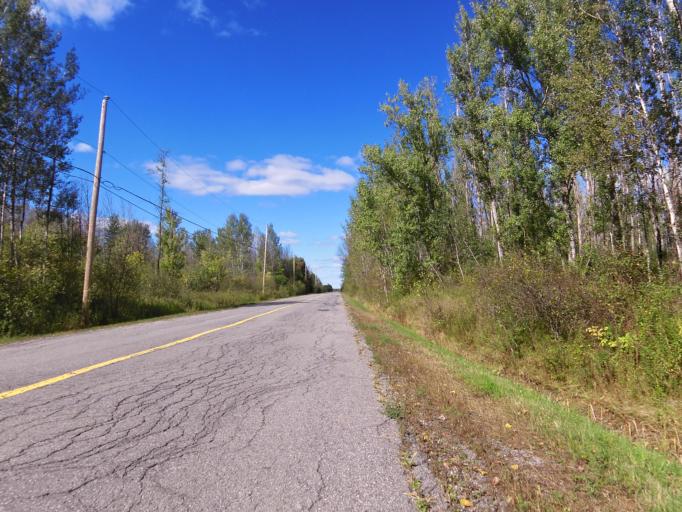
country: CA
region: Ontario
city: Ottawa
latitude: 45.3174
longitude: -75.4837
